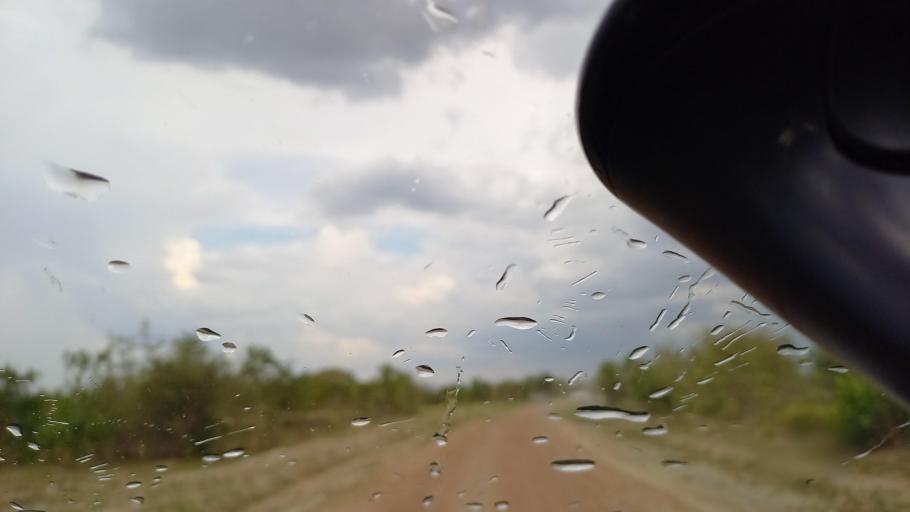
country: ZM
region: Lusaka
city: Kafue
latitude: -15.8542
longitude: 28.1171
